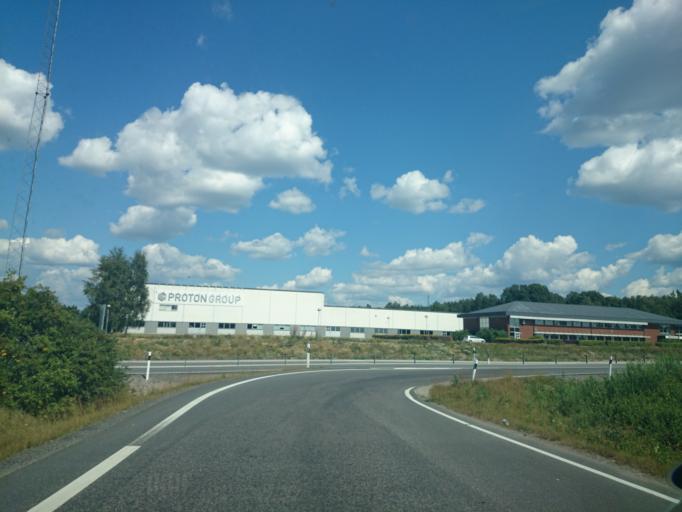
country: SE
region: Joenkoeping
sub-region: Varnamo Kommun
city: Varnamo
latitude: 57.1671
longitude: 14.0644
